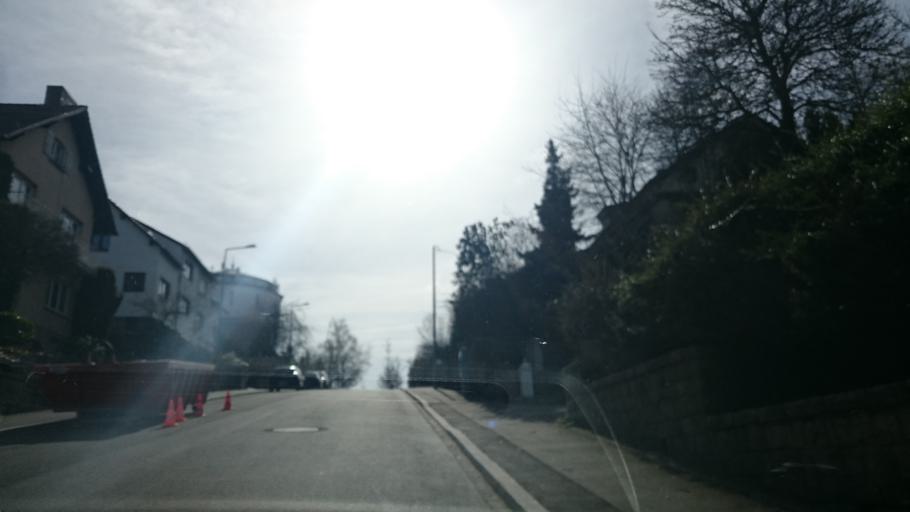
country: LU
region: Luxembourg
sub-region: Canton de Luxembourg
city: Luxembourg
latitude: 49.5875
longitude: 6.1080
